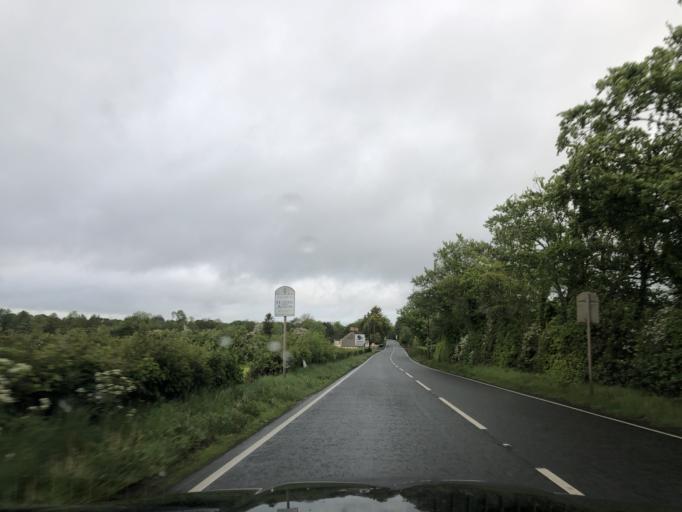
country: GB
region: Northern Ireland
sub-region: Antrim Borough
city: Antrim
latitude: 54.6736
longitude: -6.2208
